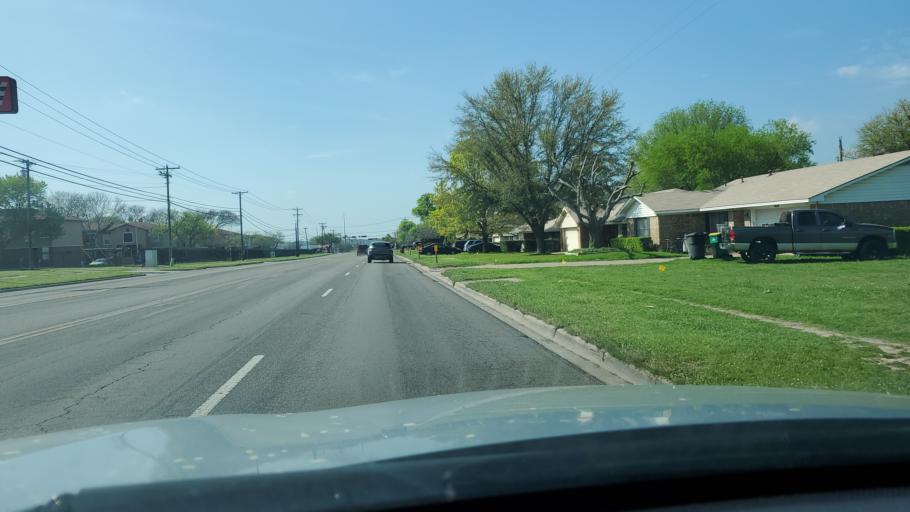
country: US
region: Texas
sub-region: Bell County
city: Temple
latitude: 31.0639
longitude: -97.3717
